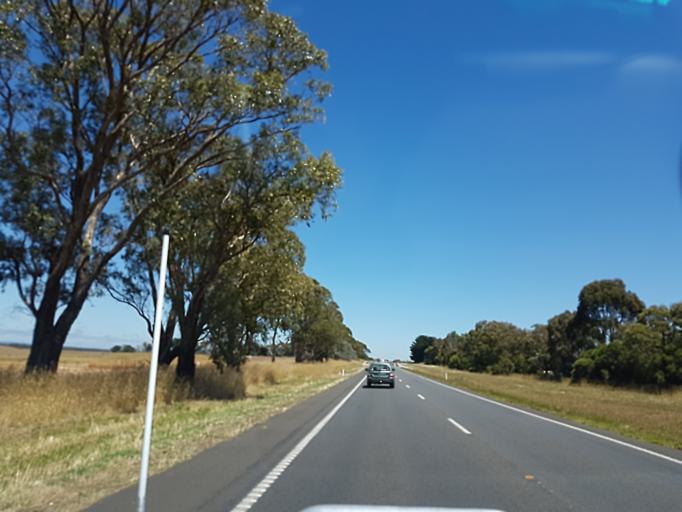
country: AU
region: Victoria
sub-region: Colac-Otway
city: Colac
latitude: -38.2933
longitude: 143.8225
